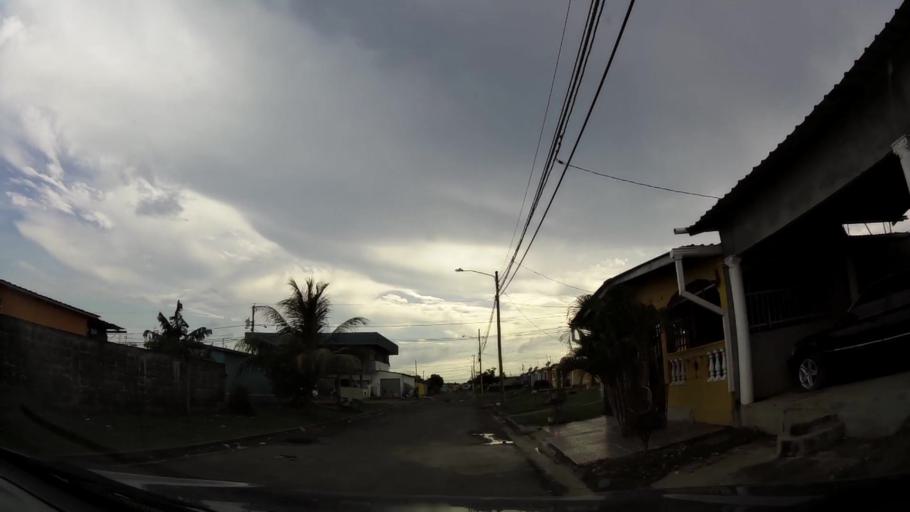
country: PA
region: Panama
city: Cabra Numero Uno
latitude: 9.0883
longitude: -79.3535
